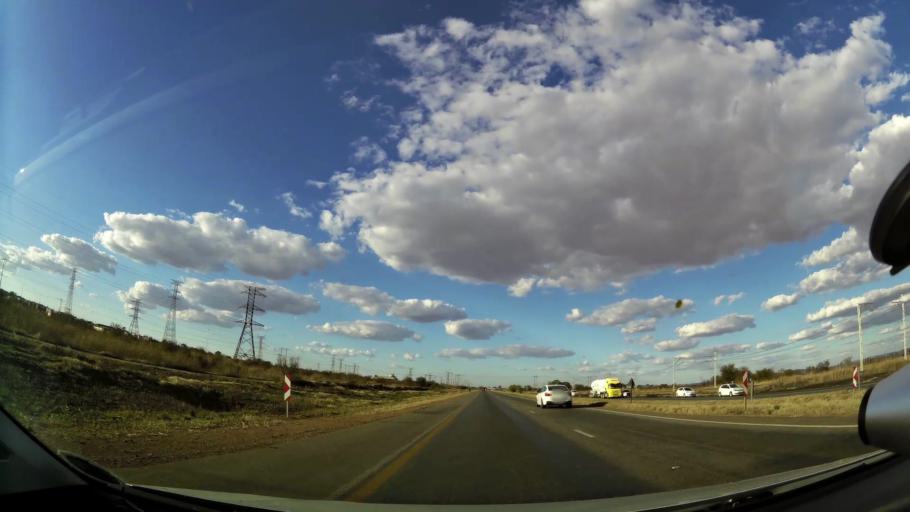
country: ZA
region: North-West
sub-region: Dr Kenneth Kaunda District Municipality
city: Potchefstroom
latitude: -26.7343
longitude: 27.0556
